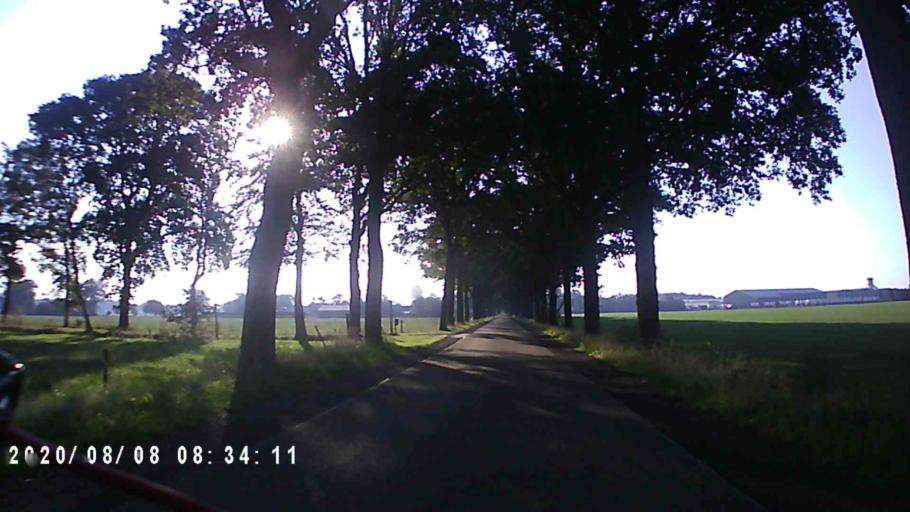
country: NL
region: Groningen
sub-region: Gemeente Leek
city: Leek
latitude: 53.0770
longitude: 6.3242
